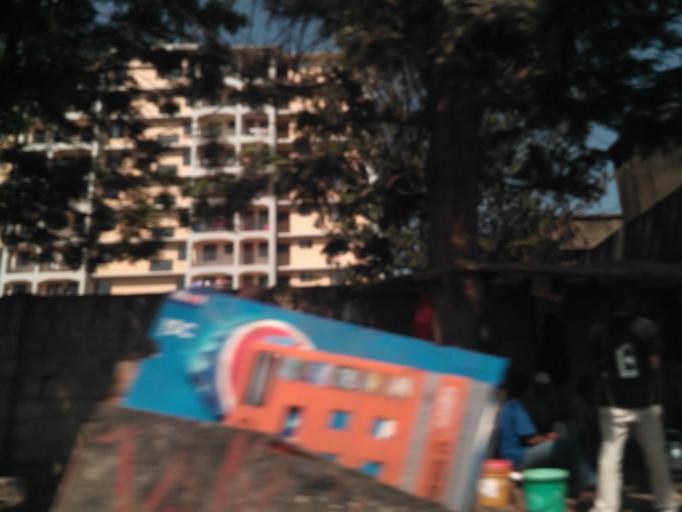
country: TZ
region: Arusha
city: Arusha
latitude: -3.3736
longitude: 36.6840
